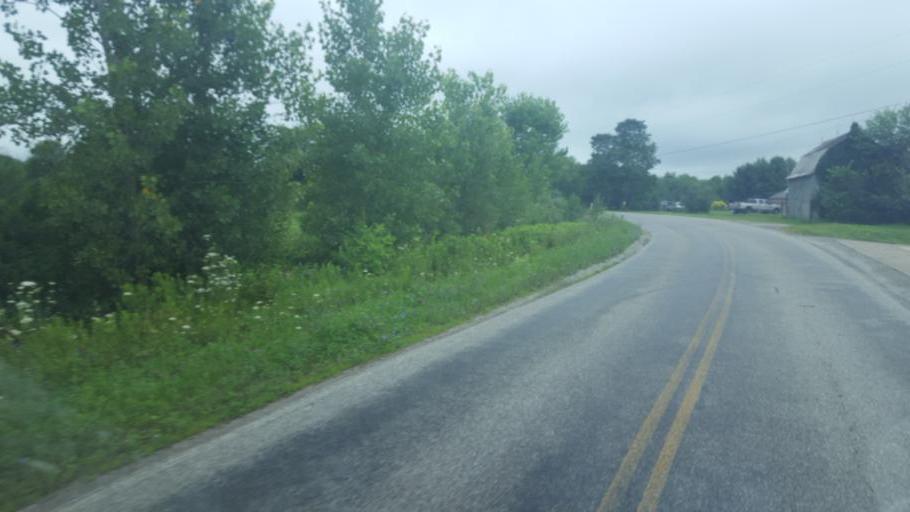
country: US
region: Ohio
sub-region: Delaware County
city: Sunbury
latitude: 40.3105
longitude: -82.8500
